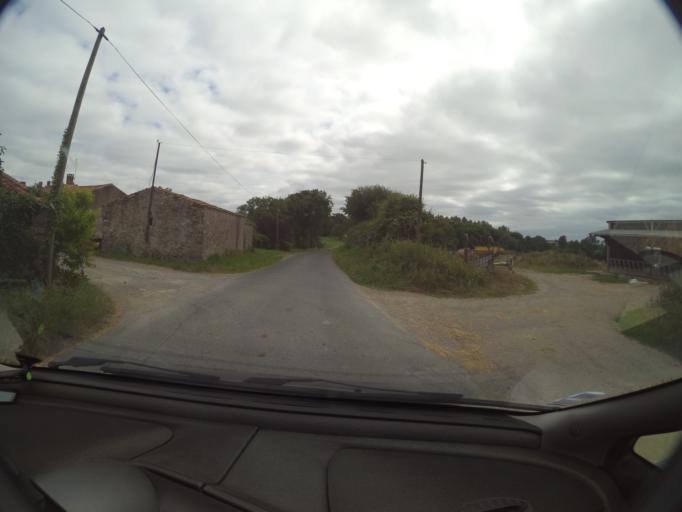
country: FR
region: Pays de la Loire
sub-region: Departement de la Vendee
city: Saint-Hilaire-de-Loulay
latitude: 47.0242
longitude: -1.3044
